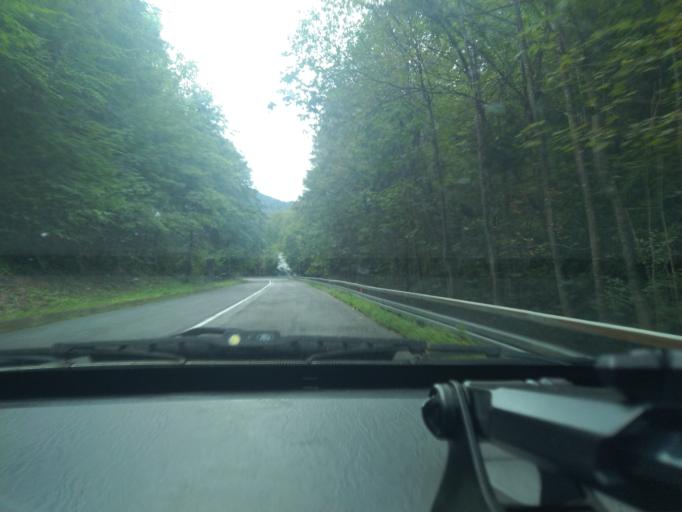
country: SK
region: Banskobystricky
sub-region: Okres Banska Bystrica
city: Banska Bystrica
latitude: 48.8224
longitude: 19.0298
